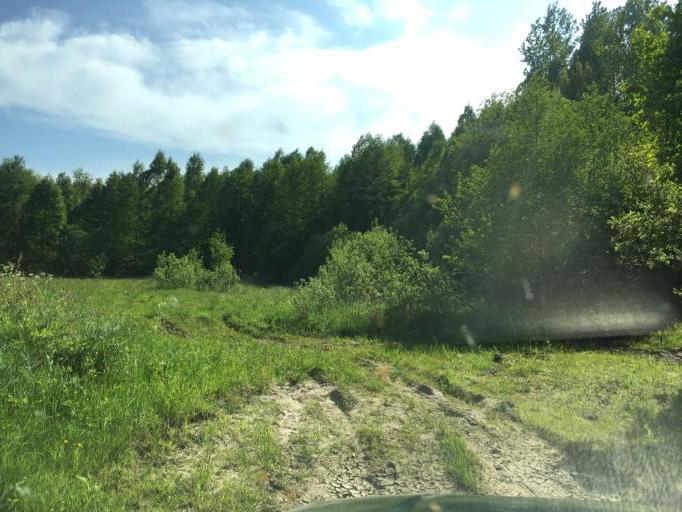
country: LV
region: Dundaga
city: Dundaga
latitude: 57.5996
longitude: 22.5055
